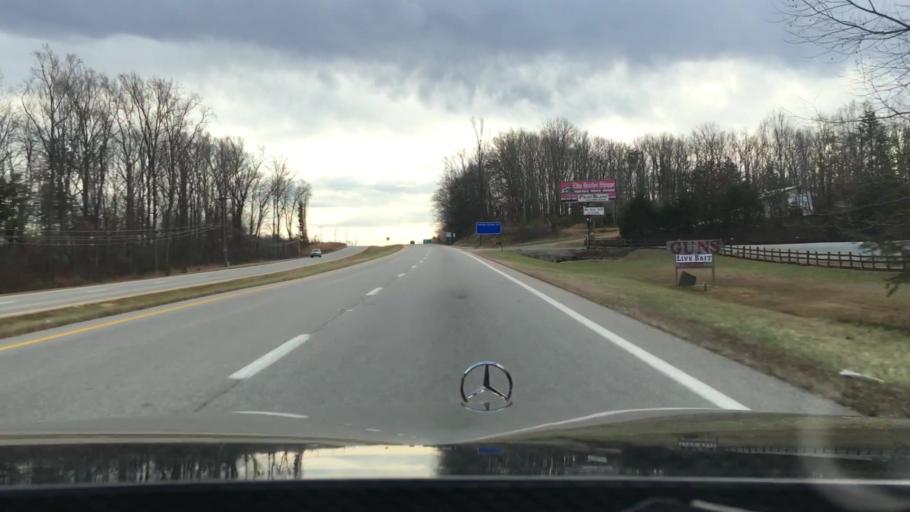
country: US
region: Virginia
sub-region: Pittsylvania County
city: Gretna
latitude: 36.9903
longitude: -79.3555
